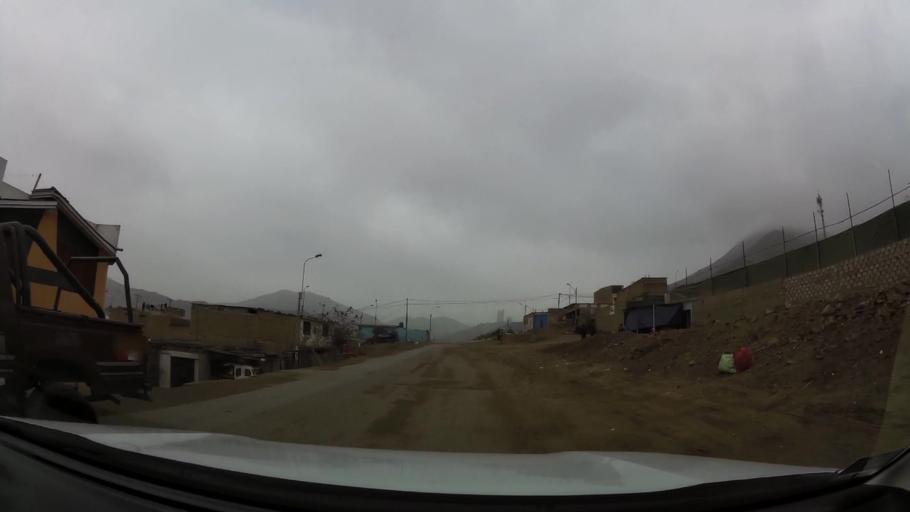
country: PE
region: Lima
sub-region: Lima
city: Cieneguilla
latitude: -12.2155
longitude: -76.9022
